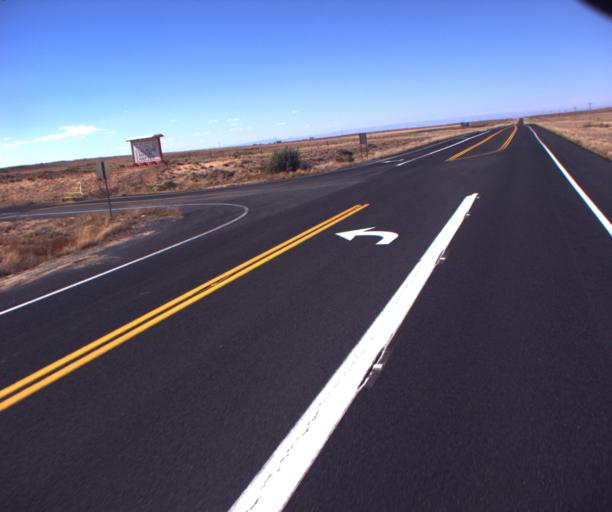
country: US
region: Arizona
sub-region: Coconino County
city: Tuba City
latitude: 35.9978
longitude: -111.0301
